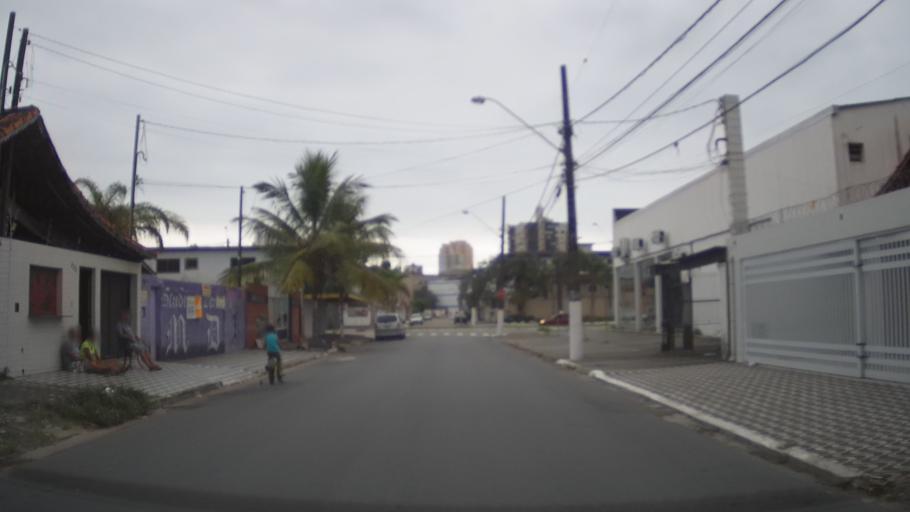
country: BR
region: Sao Paulo
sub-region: Praia Grande
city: Praia Grande
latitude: -24.0043
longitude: -46.4232
